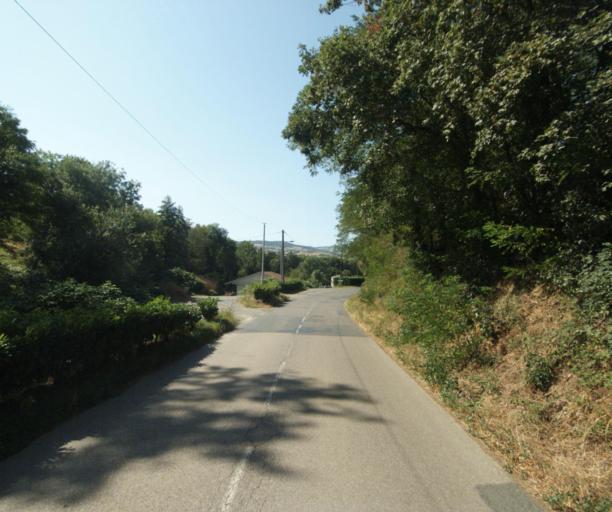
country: FR
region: Rhone-Alpes
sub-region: Departement du Rhone
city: Courzieu
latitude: 45.7492
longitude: 4.5629
